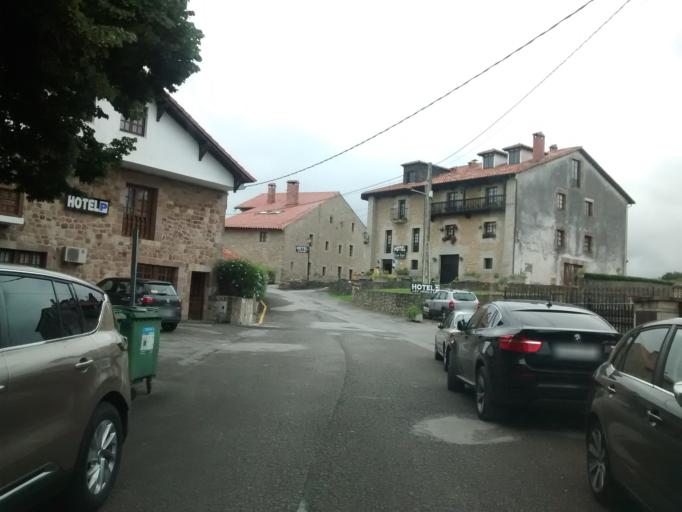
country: ES
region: Cantabria
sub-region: Provincia de Cantabria
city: Santillana
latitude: 43.3885
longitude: -4.1114
